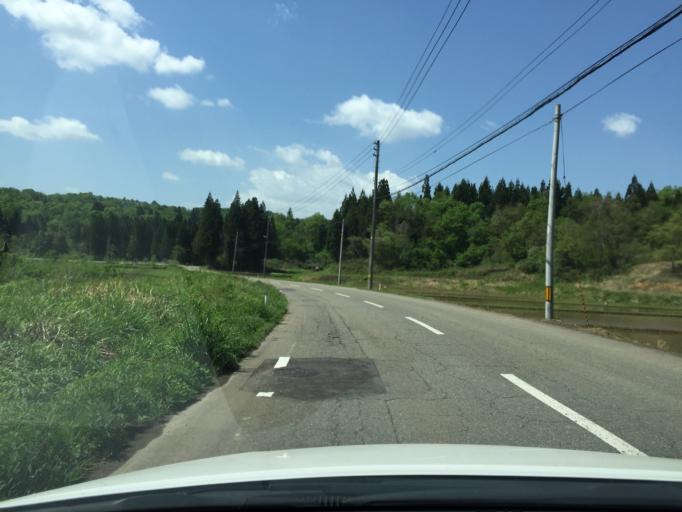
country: JP
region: Niigata
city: Tochio-honcho
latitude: 37.5071
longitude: 139.0720
